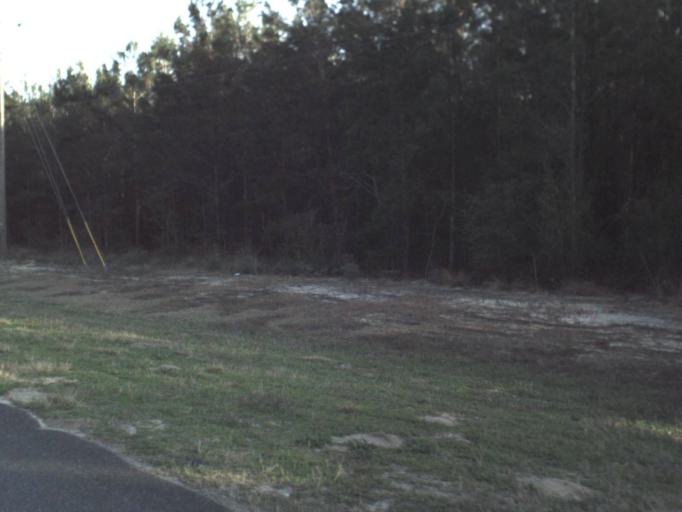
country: US
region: Florida
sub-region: Bay County
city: Lynn Haven
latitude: 30.4335
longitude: -85.6925
